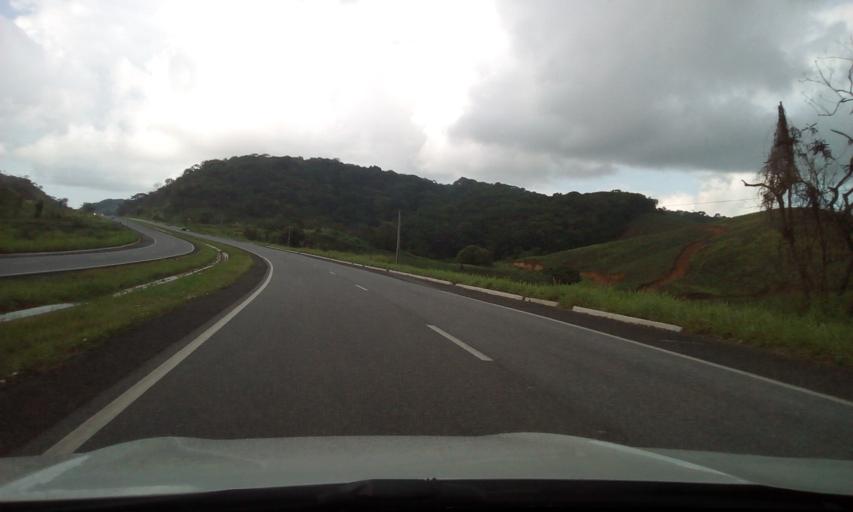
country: BR
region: Pernambuco
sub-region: Cabo De Santo Agostinho
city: Cabo
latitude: -8.2588
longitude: -35.0448
